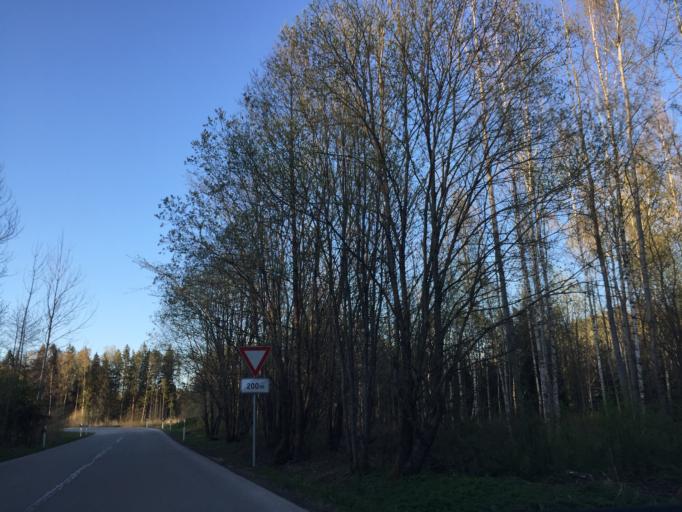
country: LV
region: Marupe
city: Marupe
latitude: 56.8289
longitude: 24.0463
